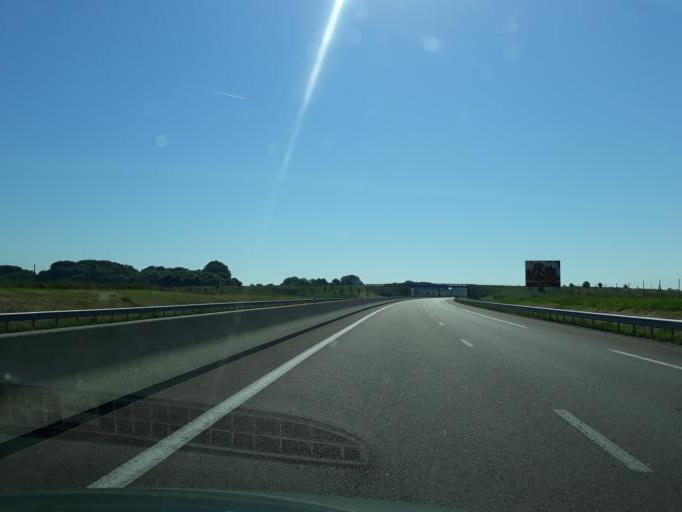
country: FR
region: Centre
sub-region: Departement du Loiret
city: Beaune-la-Rolande
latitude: 48.0957
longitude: 2.4060
